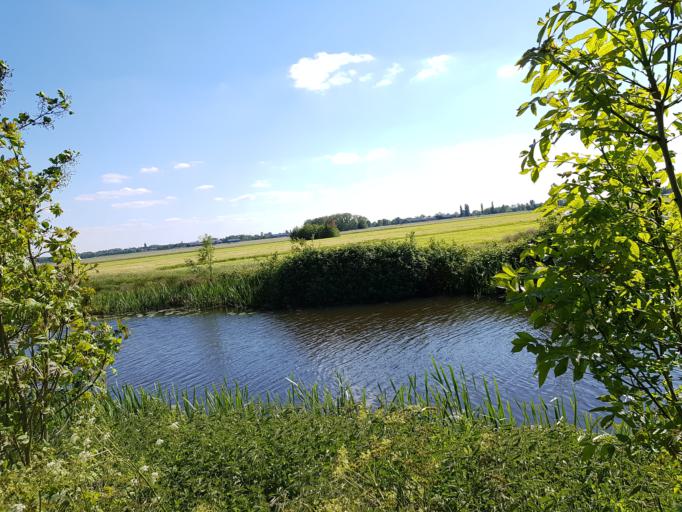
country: NL
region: South Holland
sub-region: Gemeente Schoonhoven
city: Schoonhoven
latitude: 51.9739
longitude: 4.8500
